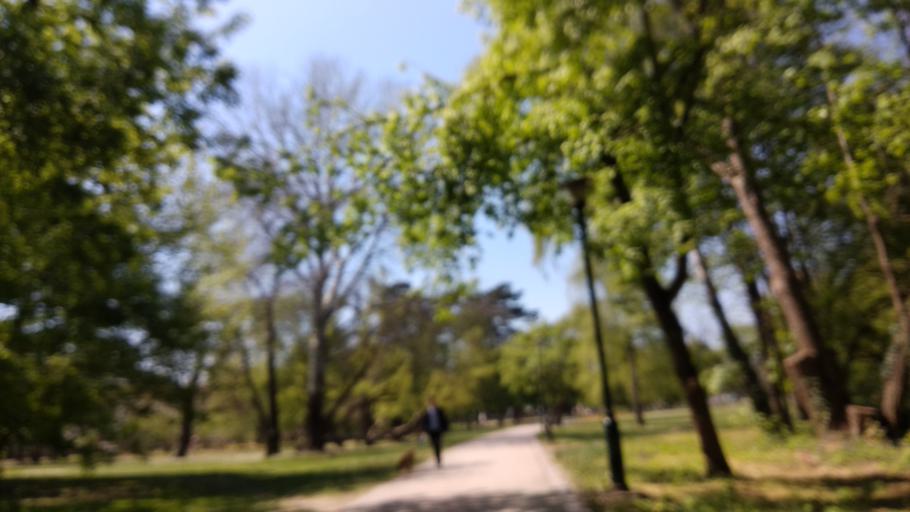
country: HU
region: Pest
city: Godollo
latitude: 47.5956
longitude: 19.3511
